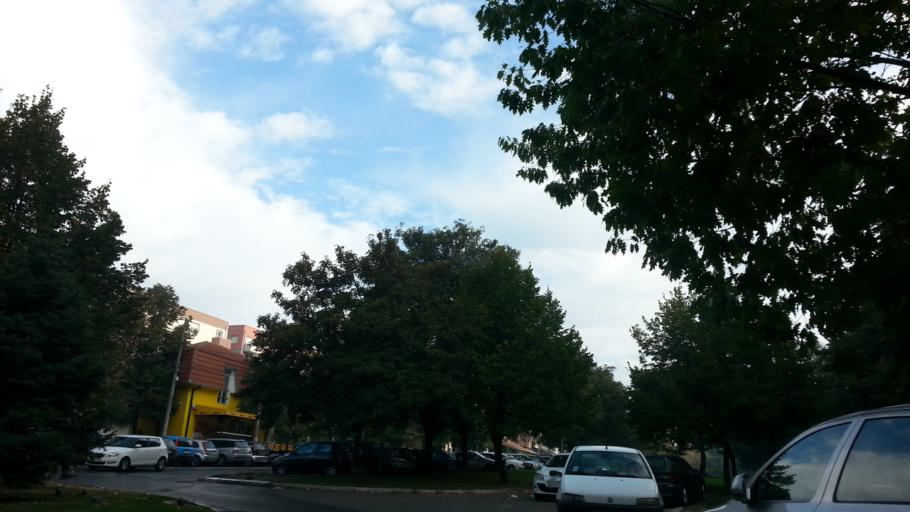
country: RS
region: Central Serbia
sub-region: Belgrade
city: Rakovica
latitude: 44.7473
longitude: 20.4307
